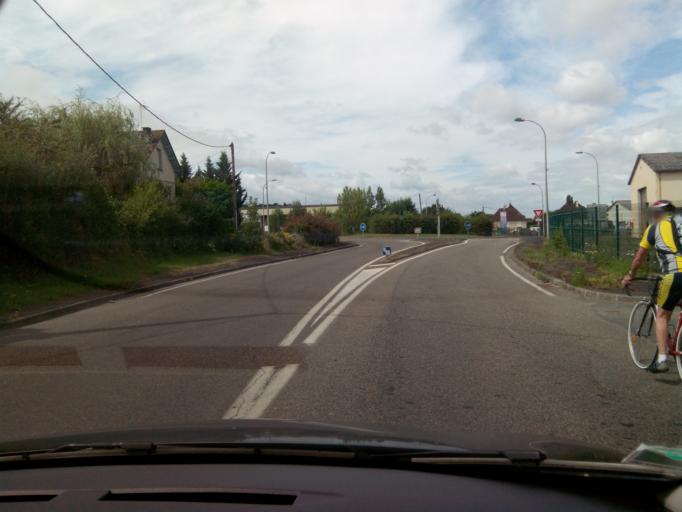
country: FR
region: Limousin
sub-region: Departement de la Correze
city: Malemort-sur-Correze
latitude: 45.1624
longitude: 1.5823
